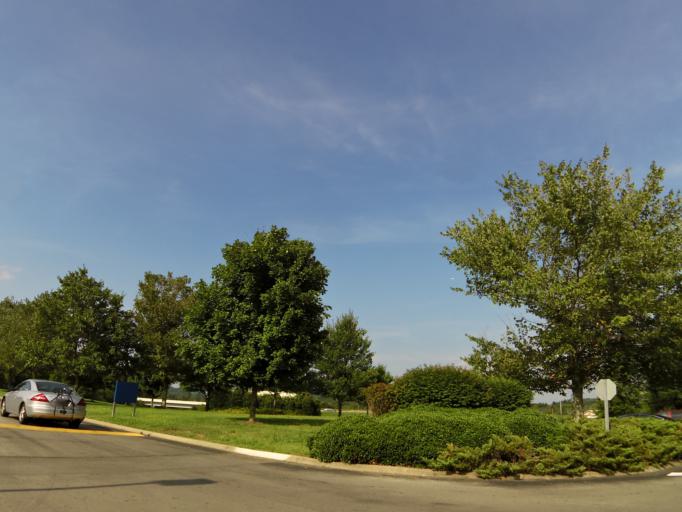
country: US
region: Tennessee
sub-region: Blount County
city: Eagleton Village
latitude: 35.8107
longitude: -83.9483
